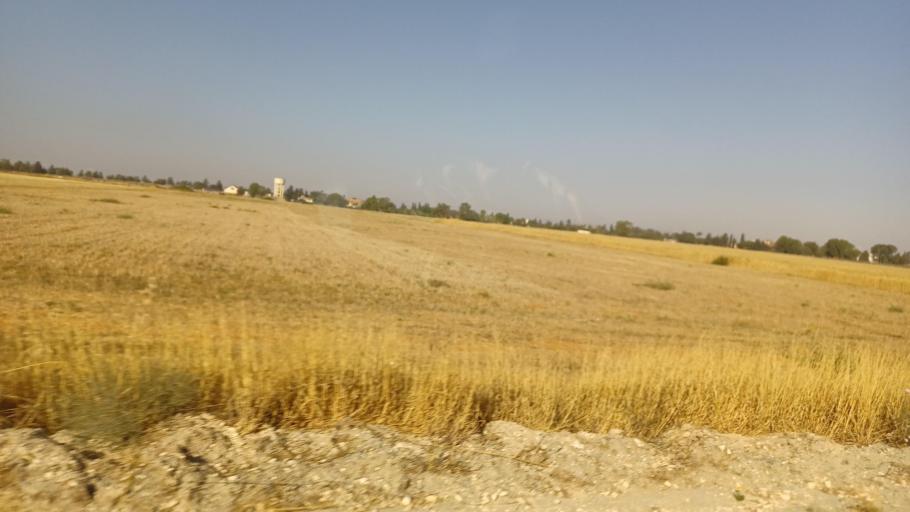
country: CY
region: Ammochostos
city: Acheritou
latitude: 35.0916
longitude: 33.8981
